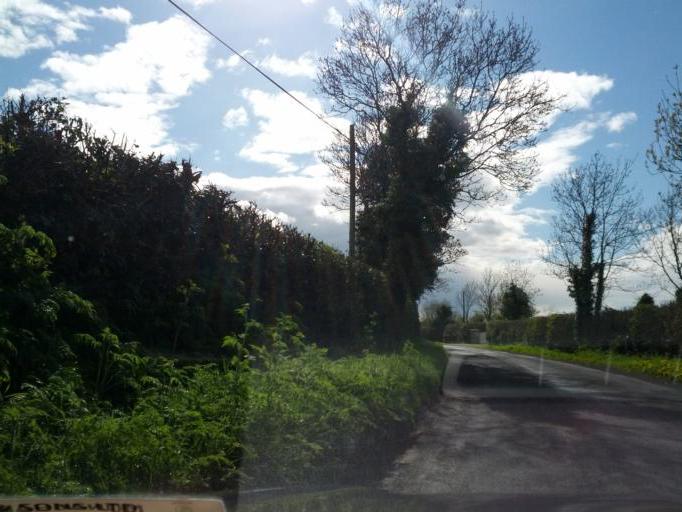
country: IE
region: Leinster
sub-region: Kildare
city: Kilcock
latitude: 53.4888
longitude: -6.6948
